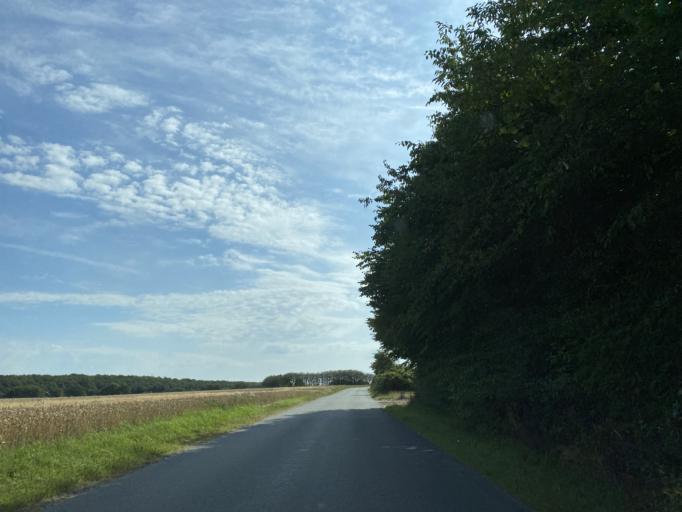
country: DK
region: Central Jutland
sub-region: Favrskov Kommune
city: Ulstrup
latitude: 56.3334
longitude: 9.7389
